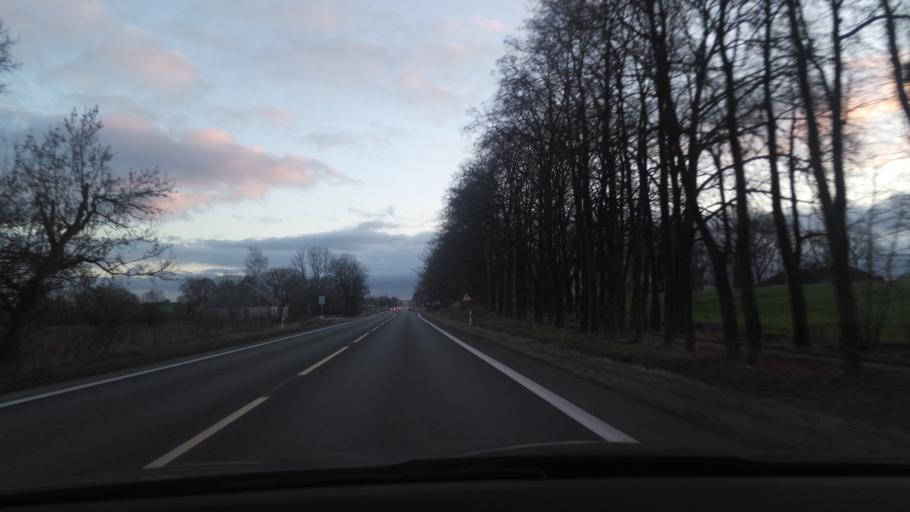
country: LT
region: Vilnius County
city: Ukmerge
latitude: 55.2167
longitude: 24.6682
